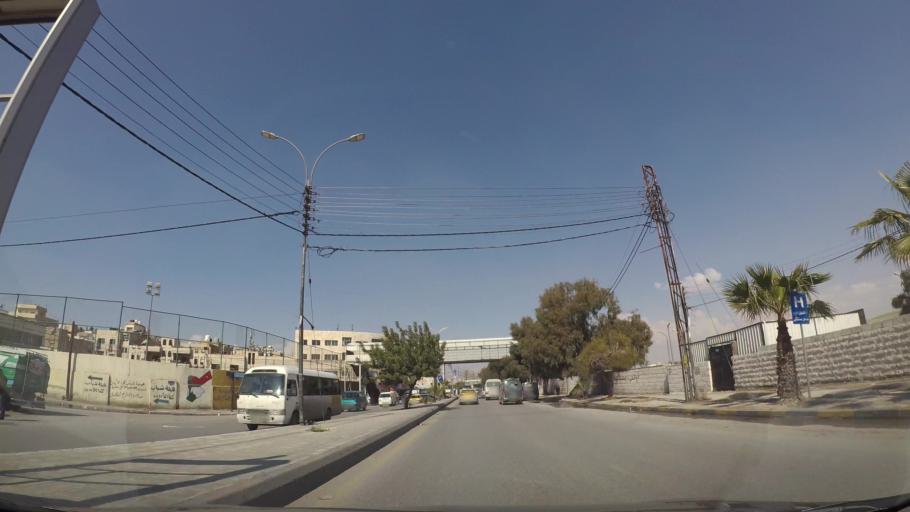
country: JO
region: Zarqa
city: Zarqa
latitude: 32.0679
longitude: 36.0967
